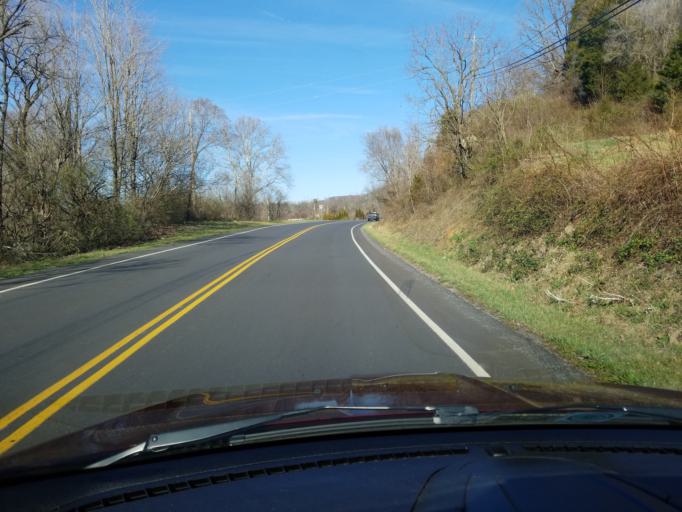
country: US
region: Virginia
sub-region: Botetourt County
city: Cloverdale
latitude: 37.3613
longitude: -79.9104
